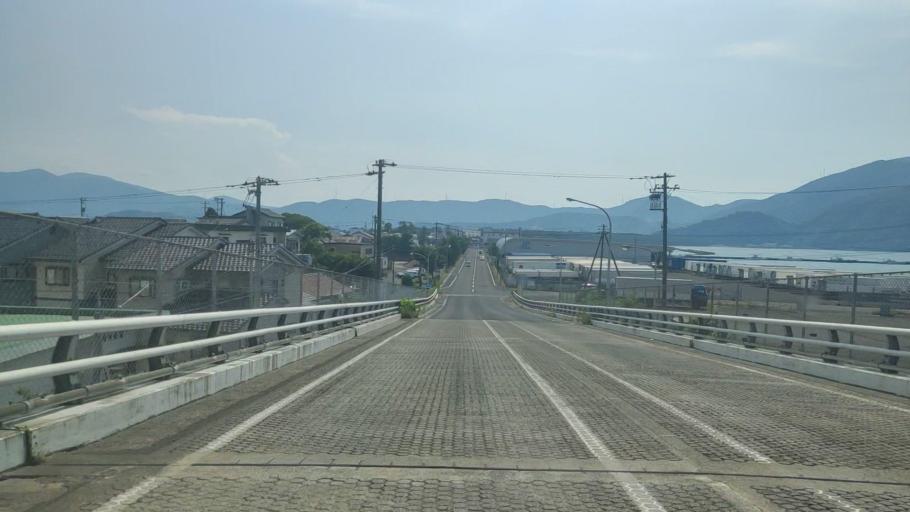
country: JP
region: Fukui
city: Tsuruga
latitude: 35.6580
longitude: 136.0650
